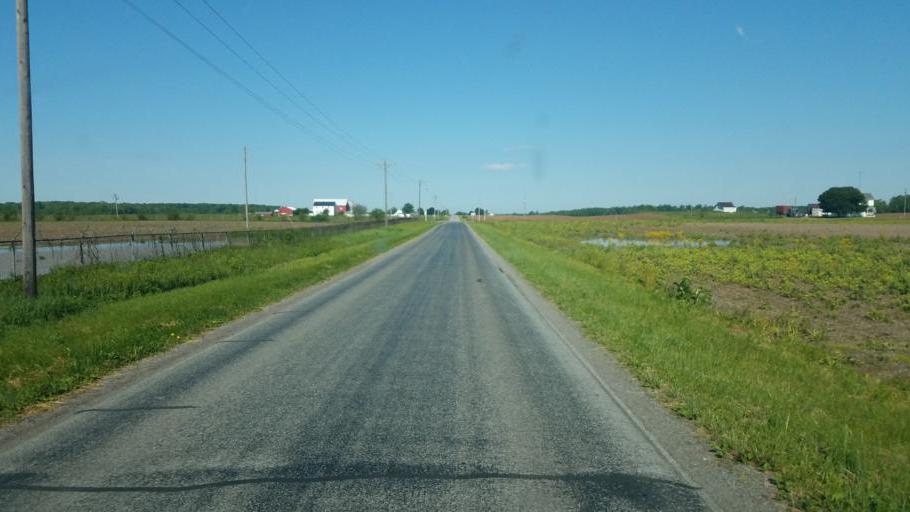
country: US
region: Ohio
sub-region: Hardin County
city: Kenton
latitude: 40.5776
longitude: -83.5884
